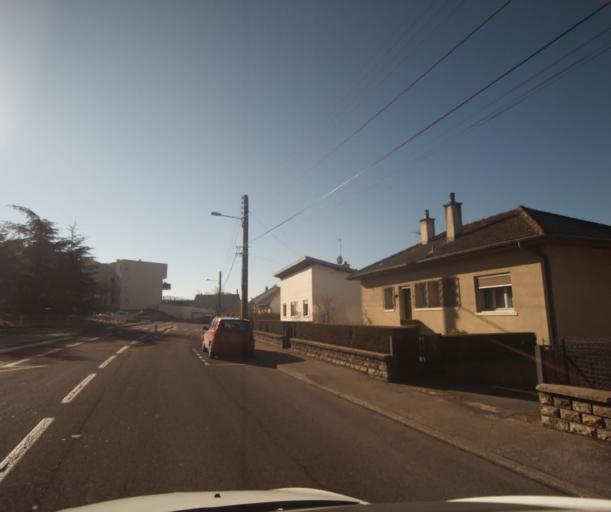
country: FR
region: Franche-Comte
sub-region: Departement du Doubs
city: Besancon
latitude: 47.2336
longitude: 5.9939
